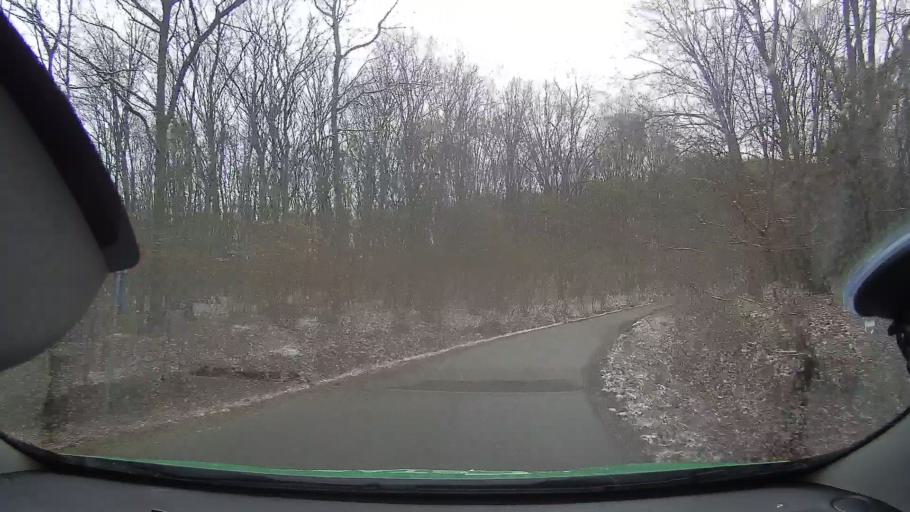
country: RO
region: Mures
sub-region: Comuna Ludus
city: Gheja
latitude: 46.4005
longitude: 24.0180
